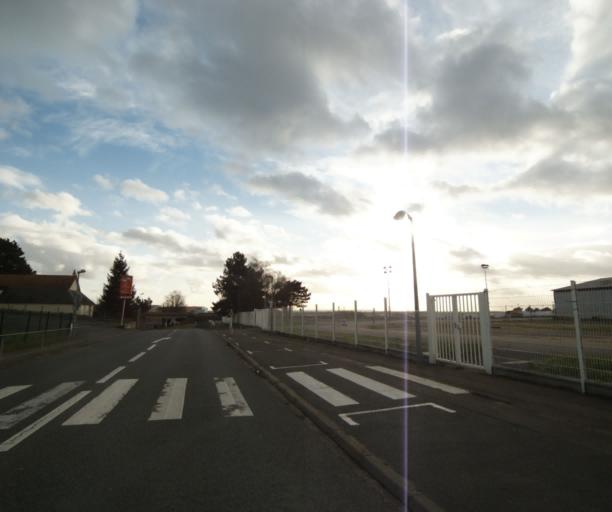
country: FR
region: Pays de la Loire
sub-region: Departement de la Sarthe
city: Arnage
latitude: 47.9592
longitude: 0.2080
